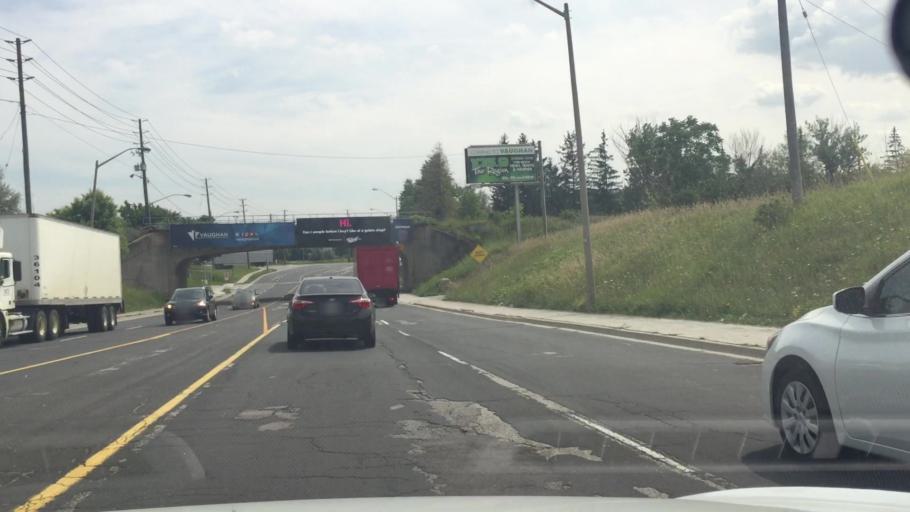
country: CA
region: Ontario
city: Concord
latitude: 43.7805
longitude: -79.5212
